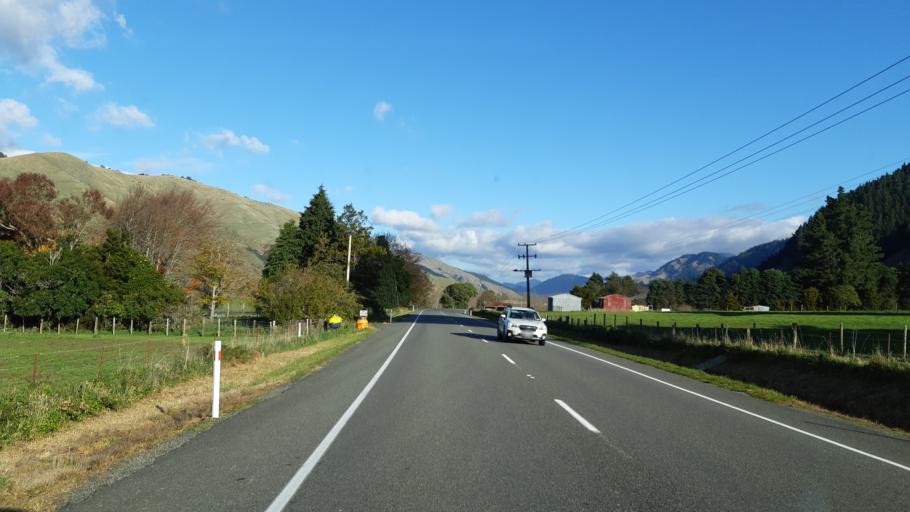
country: NZ
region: Marlborough
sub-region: Marlborough District
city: Picton
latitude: -41.3010
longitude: 173.7704
